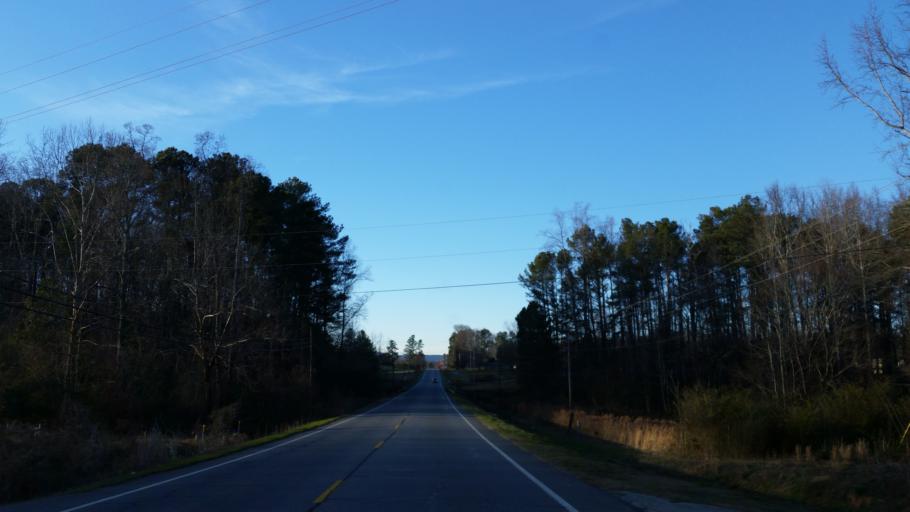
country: US
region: Georgia
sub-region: Whitfield County
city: Dalton
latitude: 34.6372
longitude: -84.9635
